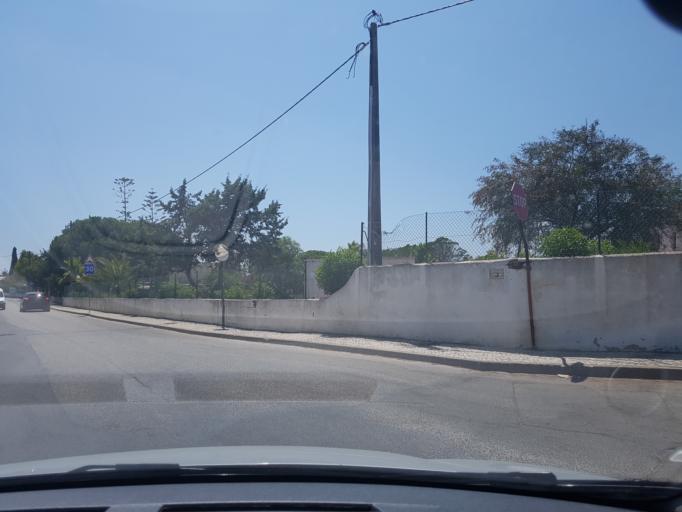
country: PT
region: Faro
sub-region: Lagoa
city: Carvoeiro
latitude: 37.0998
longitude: -8.4576
